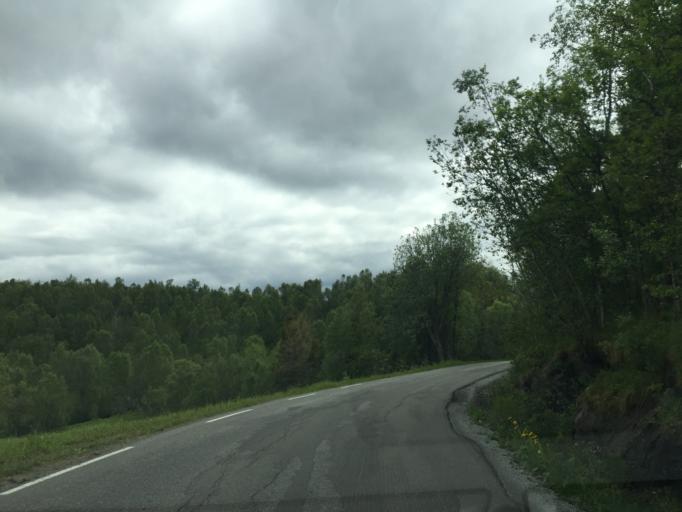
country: NO
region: Nordland
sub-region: Bodo
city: Loding
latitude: 67.3116
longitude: 14.6415
